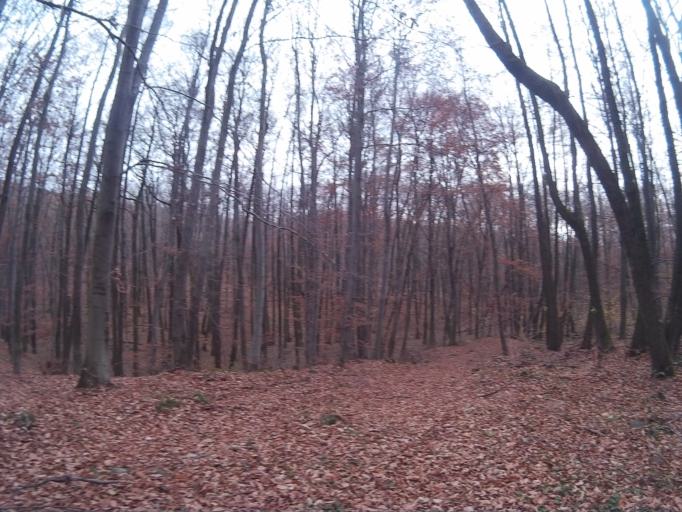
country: HU
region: Veszprem
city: Tapolca
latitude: 46.9520
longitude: 17.4971
